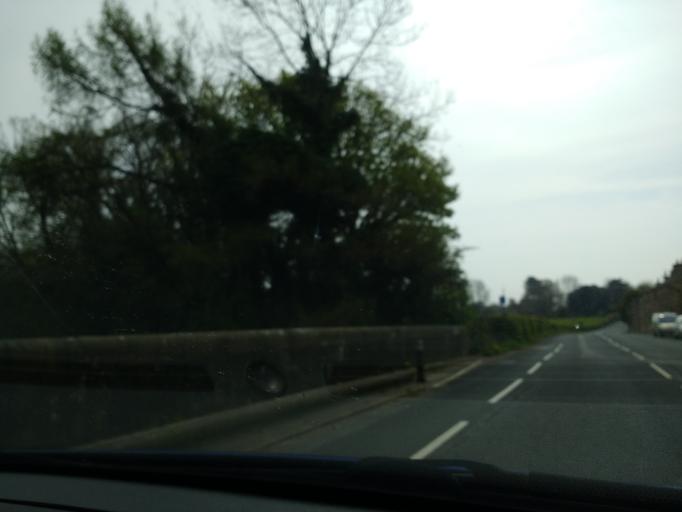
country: GB
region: England
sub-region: Lancashire
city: Lancaster
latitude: 54.0272
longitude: -2.8062
